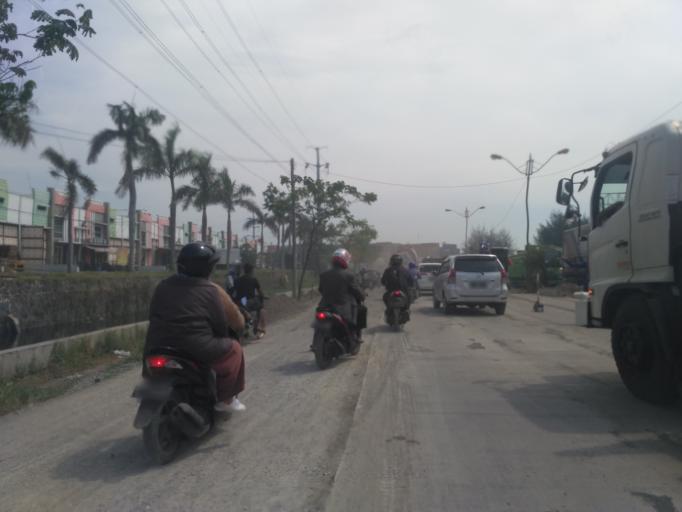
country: ID
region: Central Java
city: Semarang
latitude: -6.9544
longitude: 110.4127
